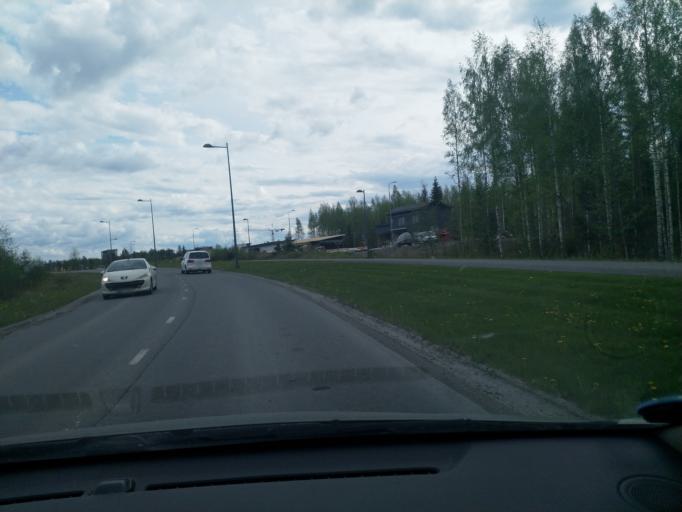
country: FI
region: Pirkanmaa
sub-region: Tampere
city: Tampere
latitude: 61.4453
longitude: 23.8062
